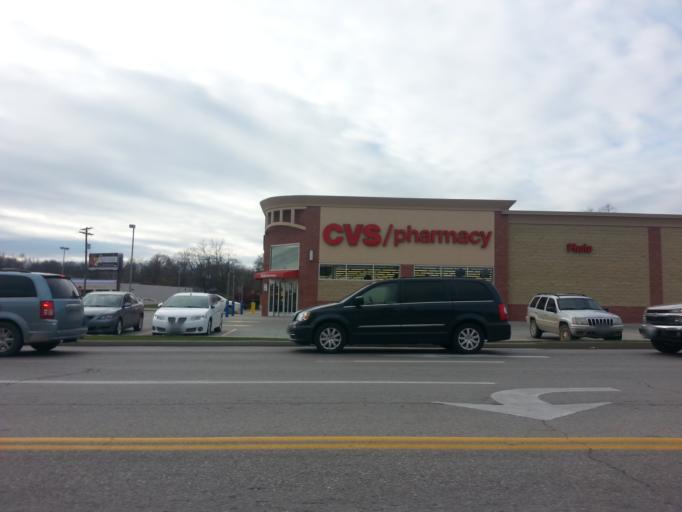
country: US
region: Missouri
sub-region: Marion County
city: Hannibal
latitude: 39.7136
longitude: -91.3918
